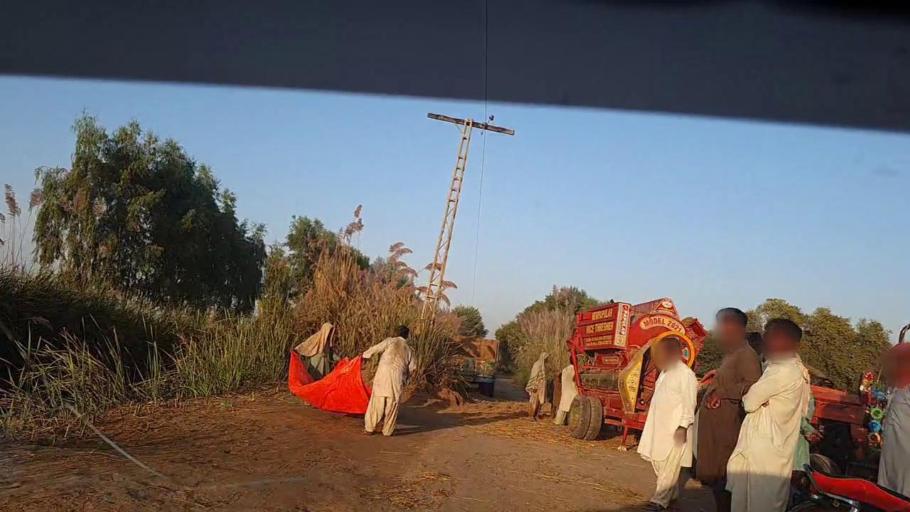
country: PK
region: Sindh
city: Ratodero
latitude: 27.8929
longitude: 68.2228
